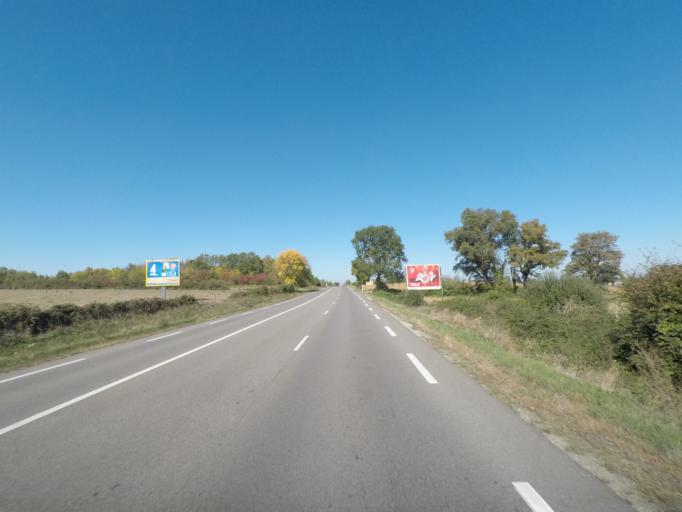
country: FR
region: Rhone-Alpes
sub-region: Departement de l'Ain
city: Viriat
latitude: 46.2368
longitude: 5.1963
